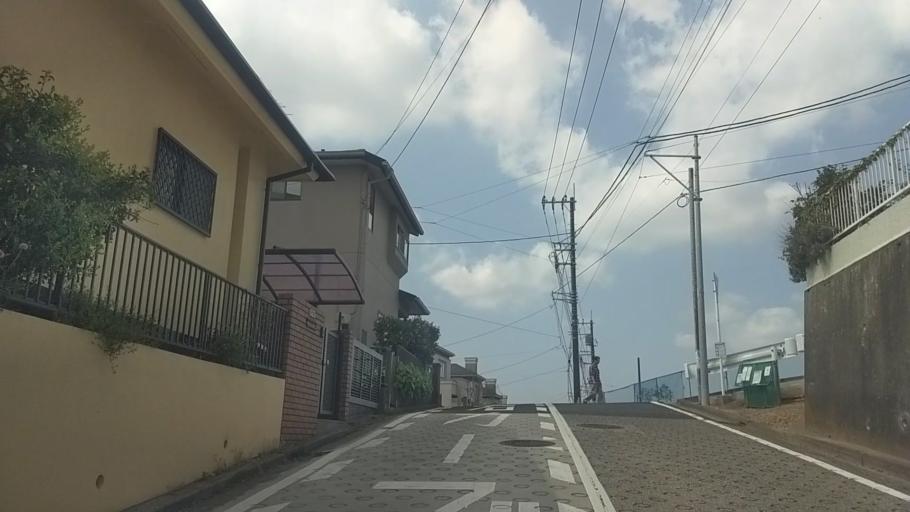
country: JP
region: Kanagawa
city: Yokohama
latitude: 35.3777
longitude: 139.6042
